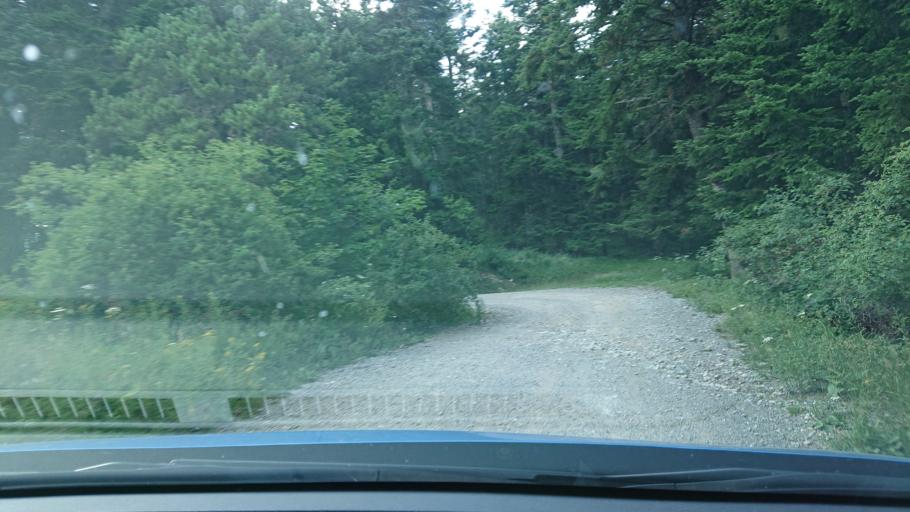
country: FR
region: Rhone-Alpes
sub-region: Departement de l'Isere
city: Mens
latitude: 44.7913
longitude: 5.8850
